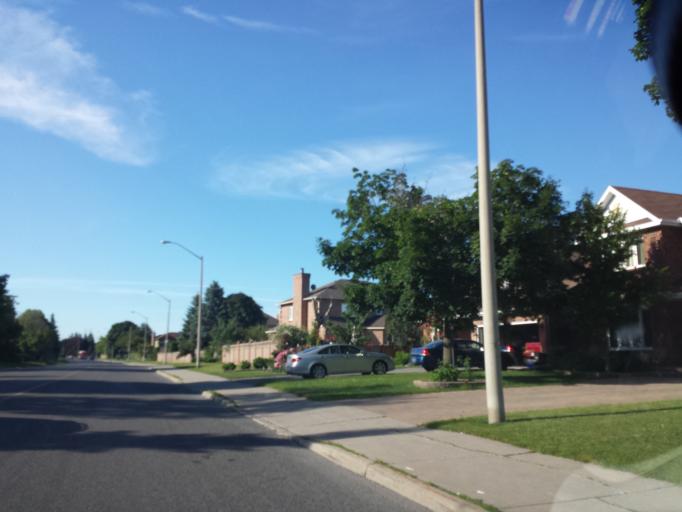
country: CA
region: Ontario
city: Bells Corners
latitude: 45.3427
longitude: -75.7733
